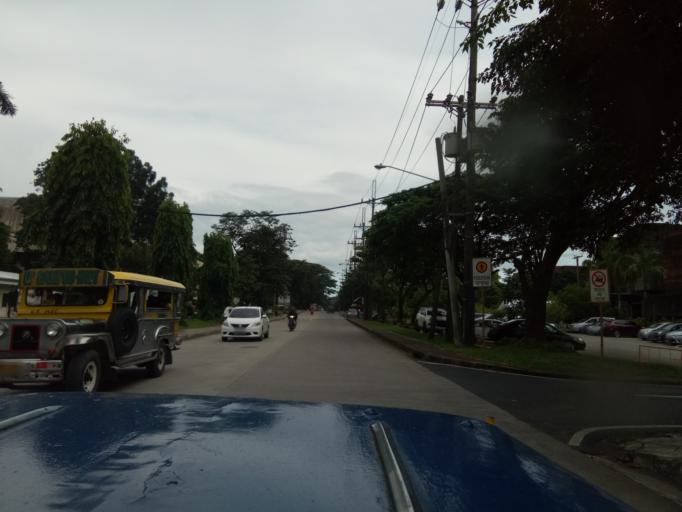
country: PH
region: Metro Manila
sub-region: Quezon City
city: Quezon City
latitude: 14.6575
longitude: 121.0656
